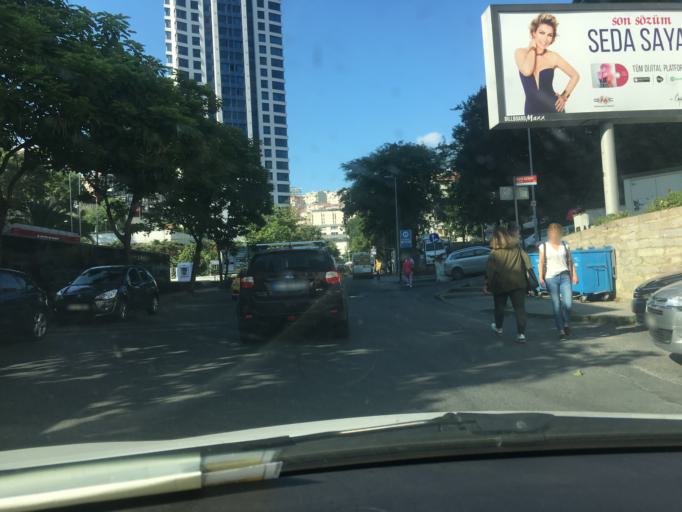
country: TR
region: Istanbul
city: Sisli
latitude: 41.0562
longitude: 28.9996
